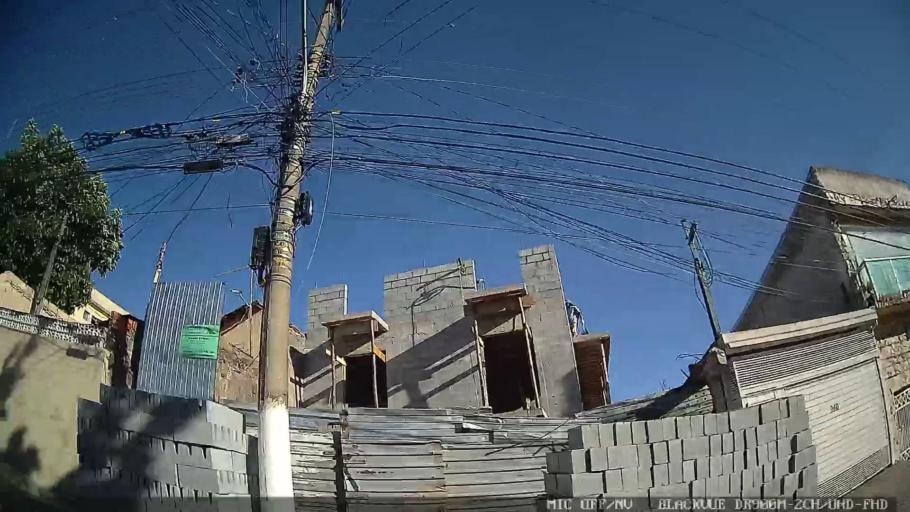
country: BR
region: Sao Paulo
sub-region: Guarulhos
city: Guarulhos
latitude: -23.5315
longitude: -46.4962
